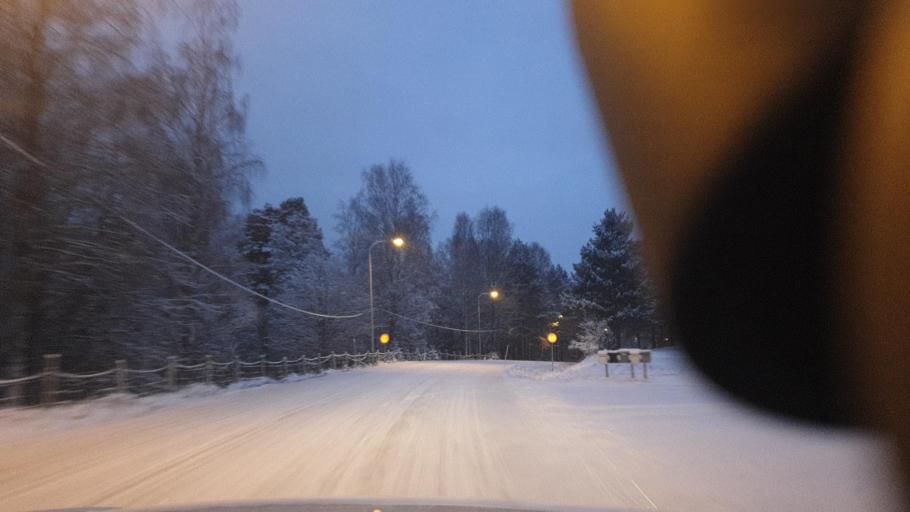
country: SE
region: Vaermland
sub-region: Eda Kommun
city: Amotfors
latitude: 59.7089
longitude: 12.1465
